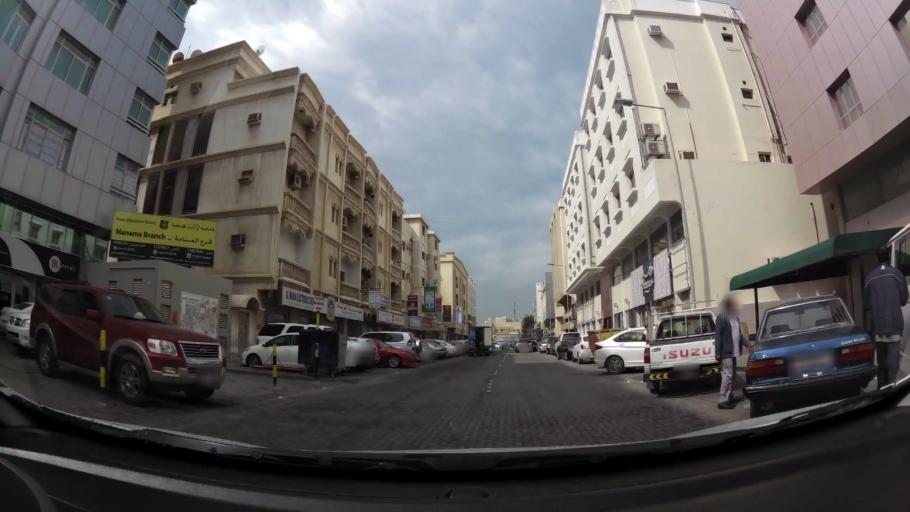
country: BH
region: Manama
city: Manama
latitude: 26.2261
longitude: 50.5950
